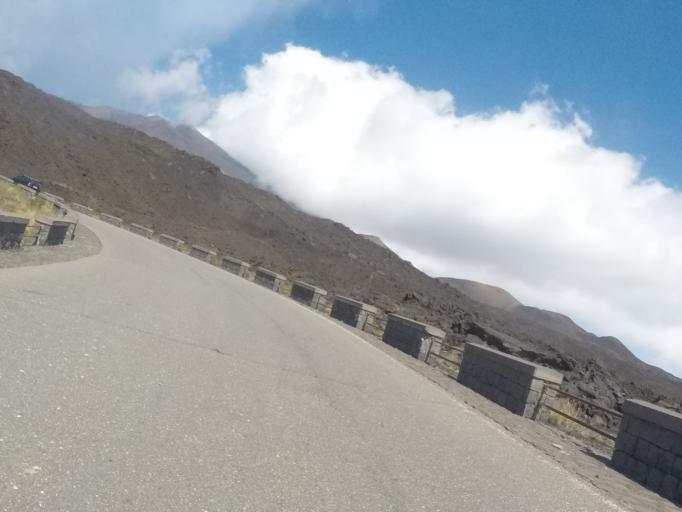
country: IT
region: Sicily
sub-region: Catania
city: Ragalna
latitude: 37.6908
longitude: 14.9952
